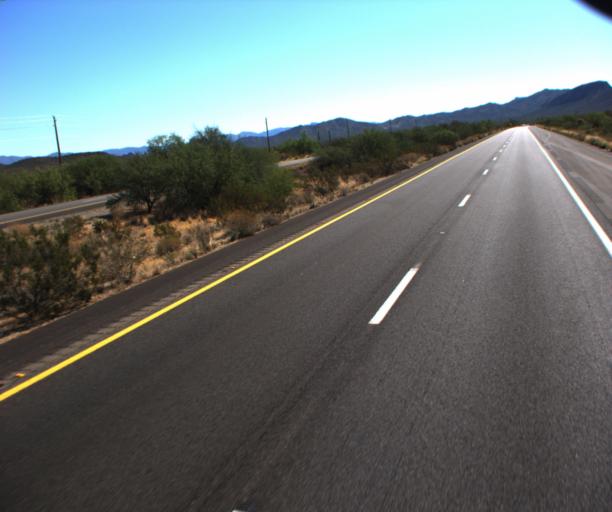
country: US
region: Arizona
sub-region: Pinal County
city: Gold Camp
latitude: 33.2575
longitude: -111.3114
